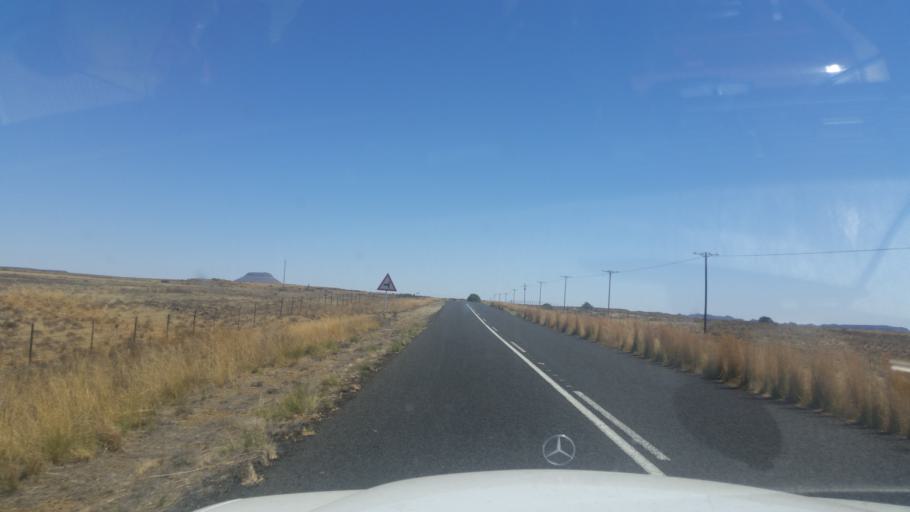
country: ZA
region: Northern Cape
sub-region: Pixley ka Seme District Municipality
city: Colesberg
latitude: -30.7021
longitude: 25.1908
